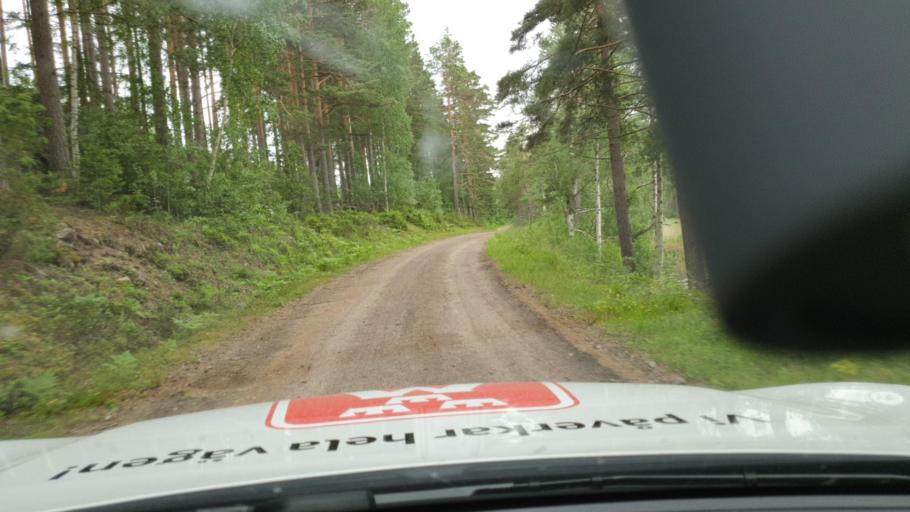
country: SE
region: OErebro
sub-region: Laxa Kommun
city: Laxa
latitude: 58.8221
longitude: 14.5467
